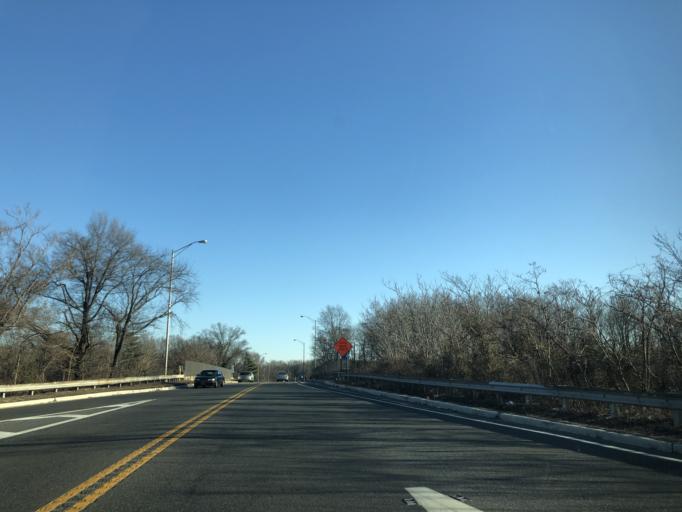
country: US
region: New Jersey
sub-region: Salem County
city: Carneys Point
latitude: 39.6838
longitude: -75.4818
